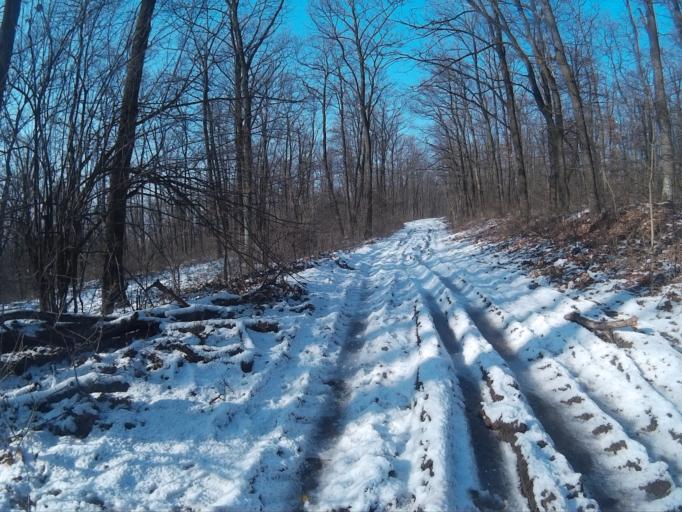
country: HU
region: Komarom-Esztergom
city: Labatlan
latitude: 47.7204
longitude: 18.4907
